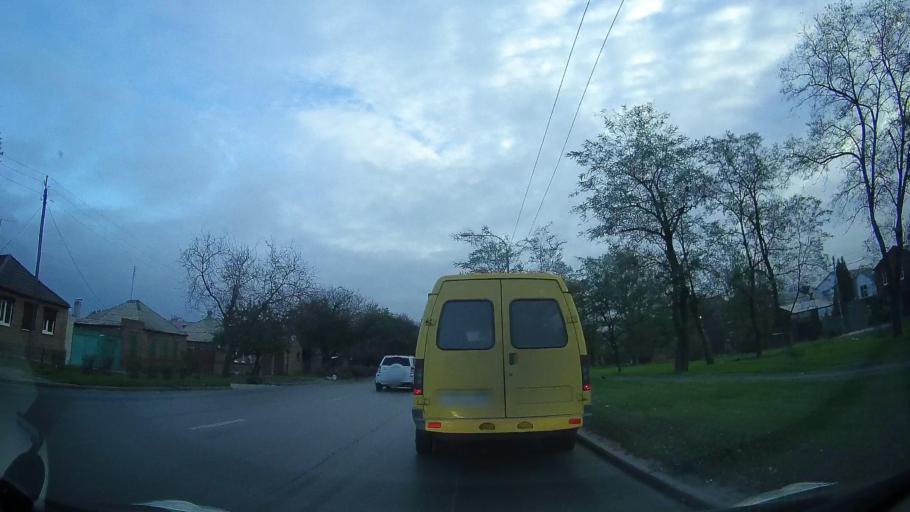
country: RU
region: Rostov
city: Rostov-na-Donu
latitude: 47.2428
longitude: 39.6435
